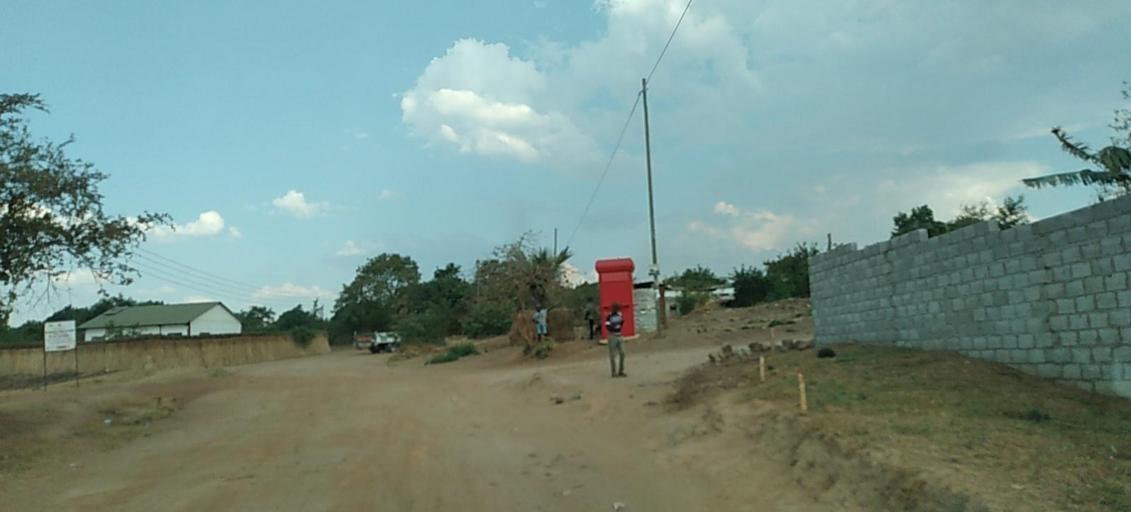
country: ZM
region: Lusaka
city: Lusaka
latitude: -15.5417
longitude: 28.2411
